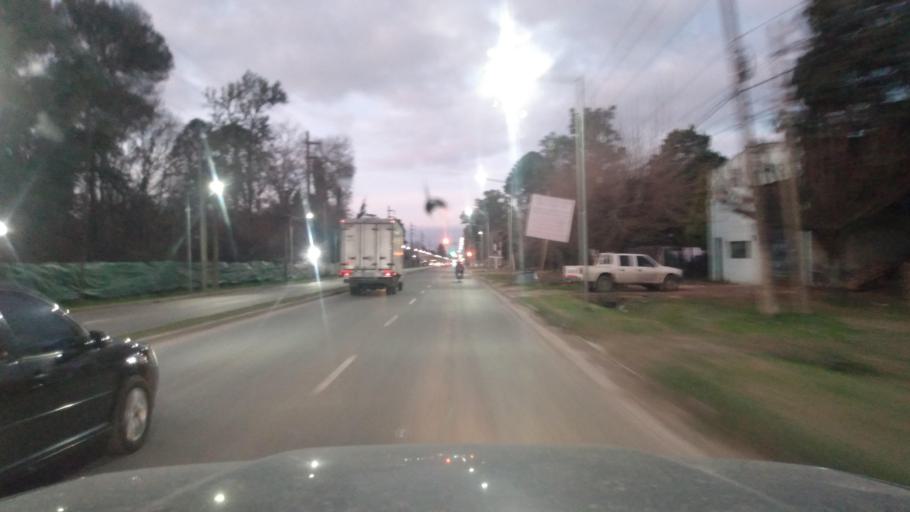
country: AR
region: Buenos Aires
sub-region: Partido de Pilar
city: Pilar
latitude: -34.4406
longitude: -58.8973
